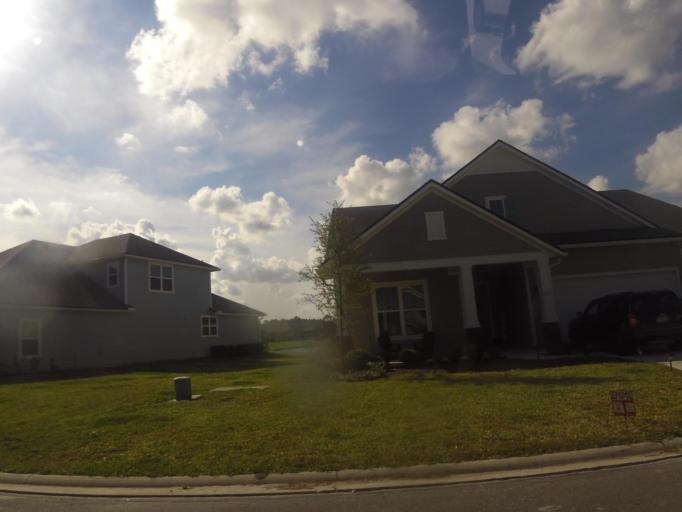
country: US
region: Florida
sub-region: Saint Johns County
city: Saint Augustine
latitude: 29.9197
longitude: -81.4925
